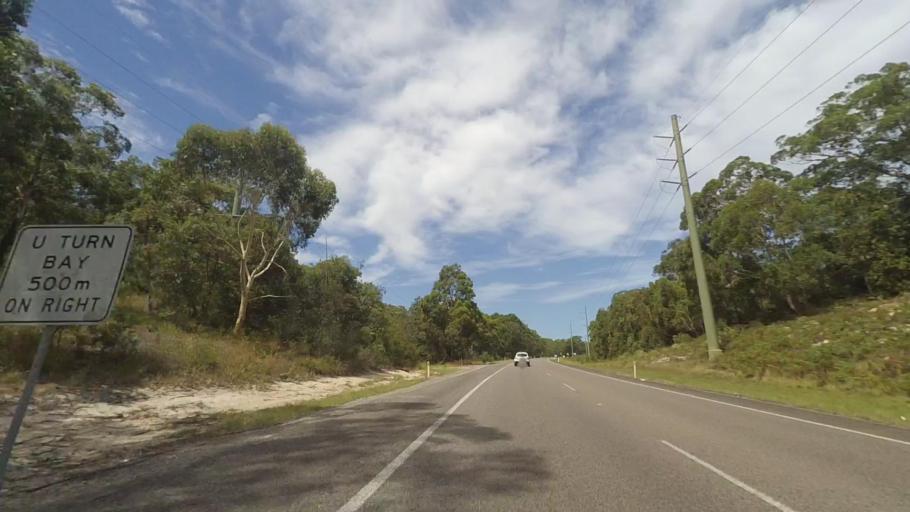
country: AU
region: New South Wales
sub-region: Port Stephens Shire
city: Medowie
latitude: -32.7868
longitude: 151.9658
